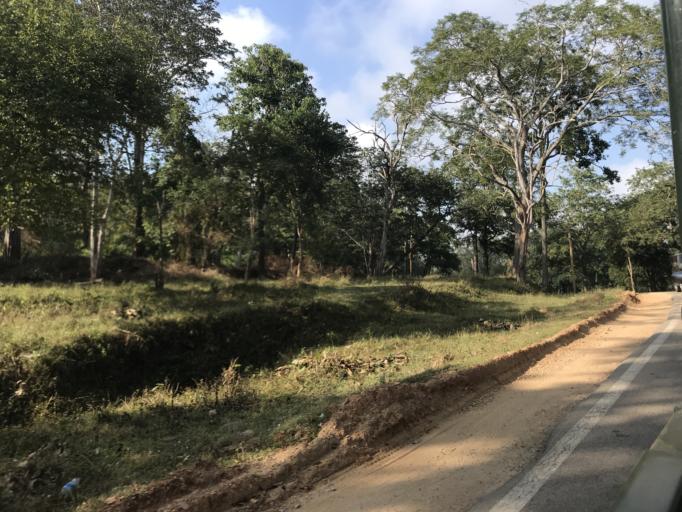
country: IN
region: Karnataka
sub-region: Mysore
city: Heggadadevankote
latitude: 11.9431
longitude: 76.2124
